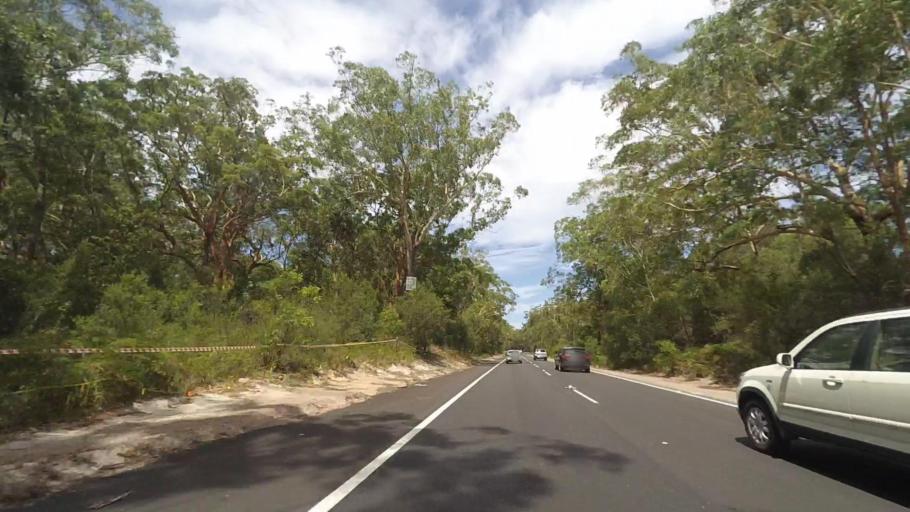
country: AU
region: New South Wales
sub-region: Port Stephens Shire
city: Anna Bay
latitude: -32.7795
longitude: 151.9917
